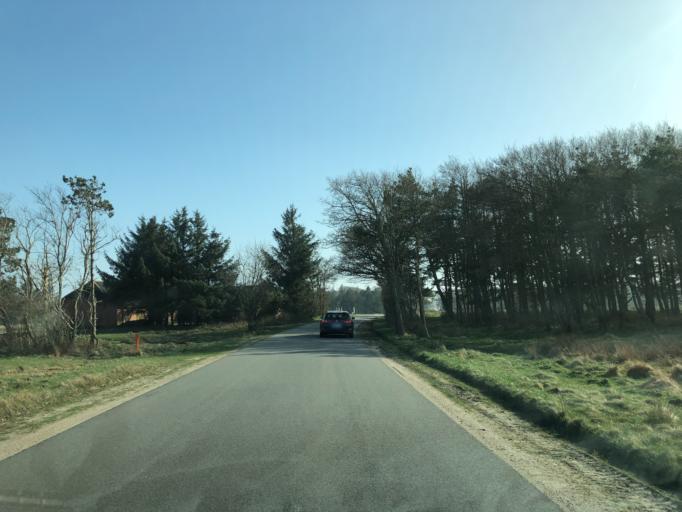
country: DK
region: South Denmark
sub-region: Varde Kommune
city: Oksbol
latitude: 55.6202
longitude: 8.1693
